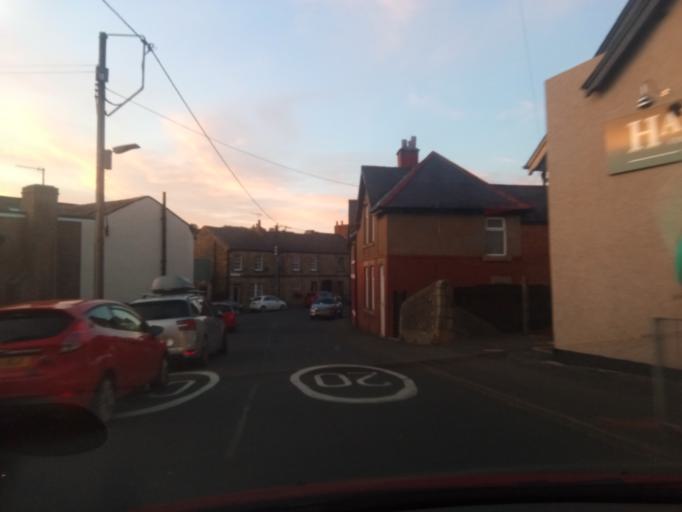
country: GB
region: England
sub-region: Northumberland
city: Bardon Mill
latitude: 54.9716
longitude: -2.2468
